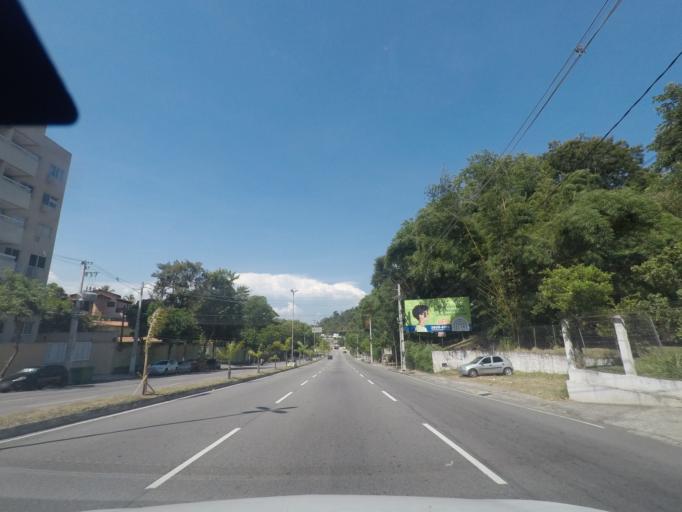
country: BR
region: Rio de Janeiro
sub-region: Niteroi
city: Niteroi
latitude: -22.9185
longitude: -43.0511
